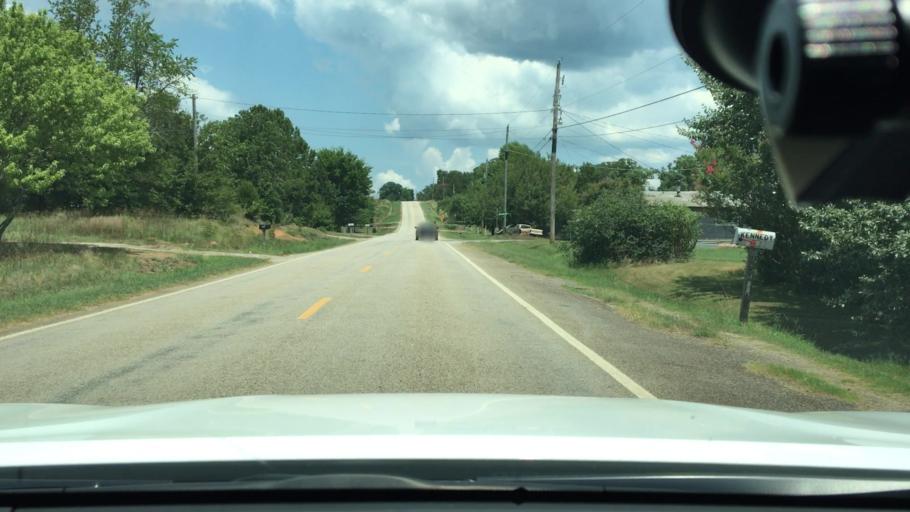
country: US
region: Arkansas
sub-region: Logan County
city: Booneville
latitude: 35.1528
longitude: -93.8770
